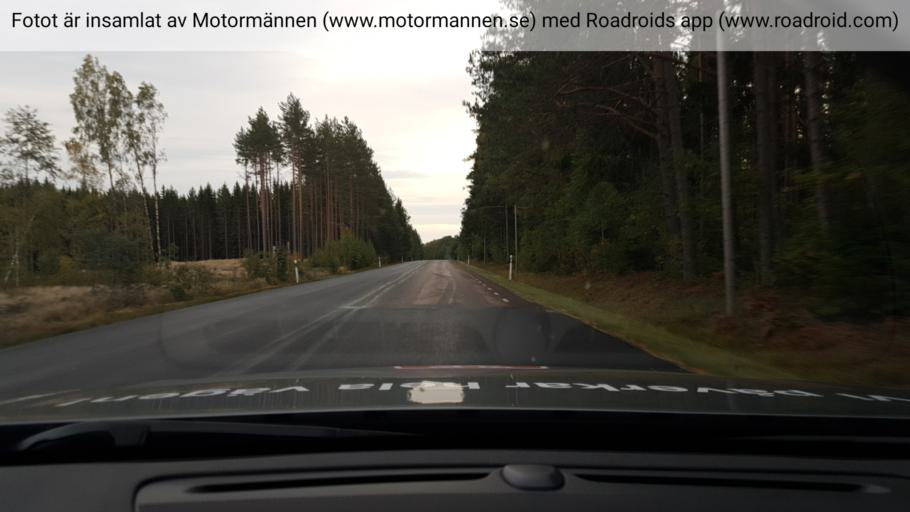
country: SE
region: Vaestra Goetaland
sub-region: Amals Kommun
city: Amal
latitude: 59.0664
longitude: 12.6534
